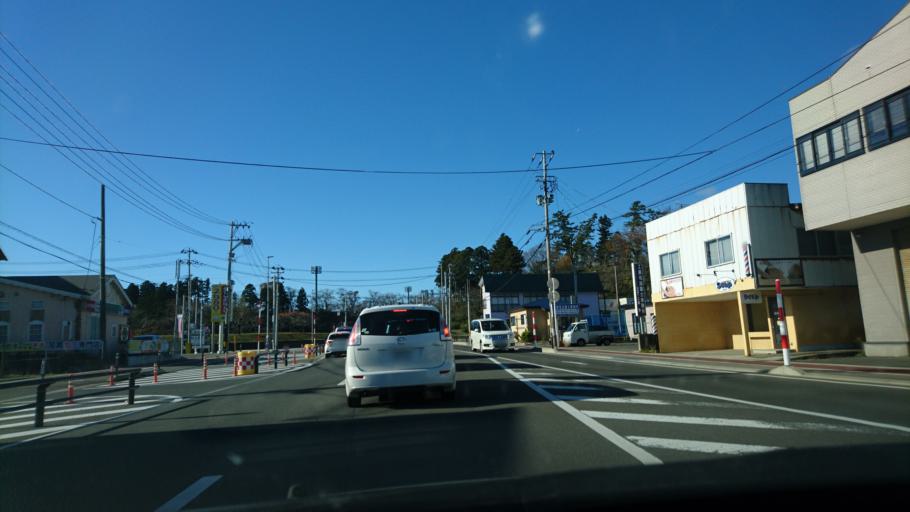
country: JP
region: Akita
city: Akita Shi
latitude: 39.3827
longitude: 140.0492
